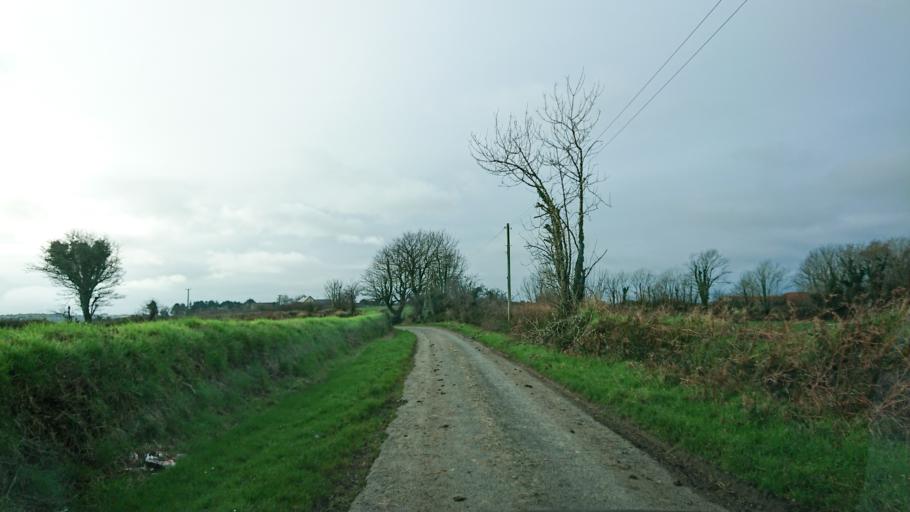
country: IE
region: Munster
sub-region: Waterford
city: Tra Mhor
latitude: 52.1946
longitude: -7.1722
